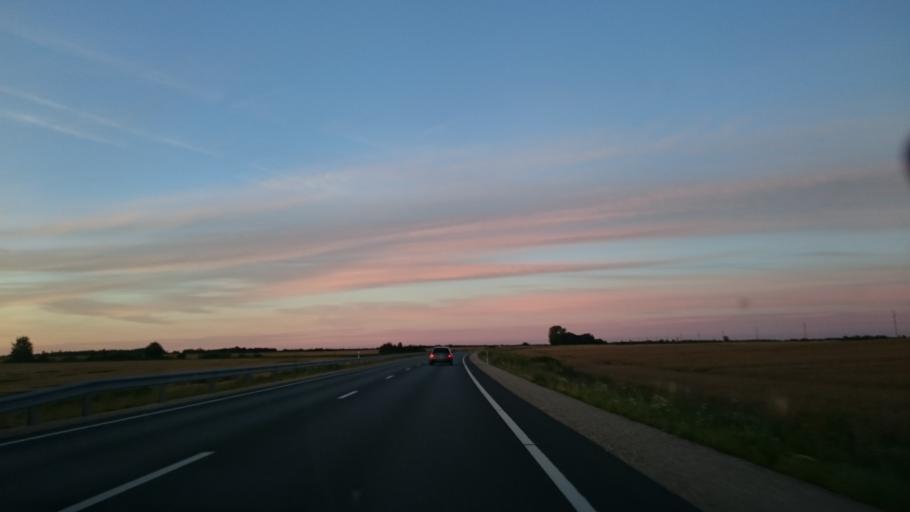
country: LV
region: Dobeles Rajons
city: Dobele
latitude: 56.7321
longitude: 23.2172
